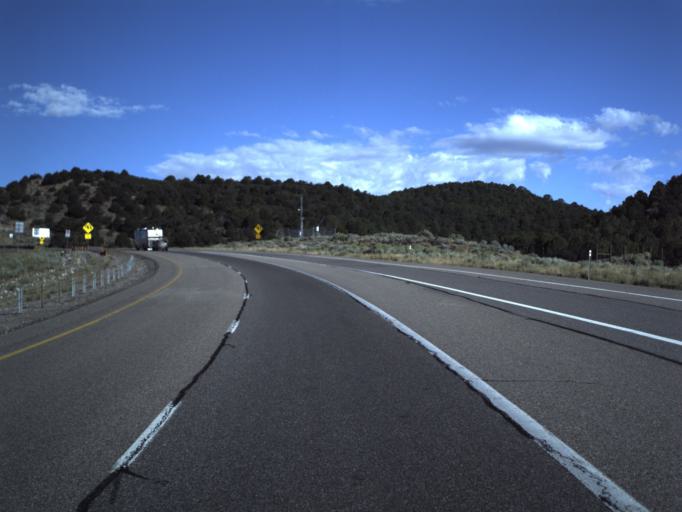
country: US
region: Utah
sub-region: Beaver County
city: Beaver
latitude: 38.5901
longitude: -112.4924
